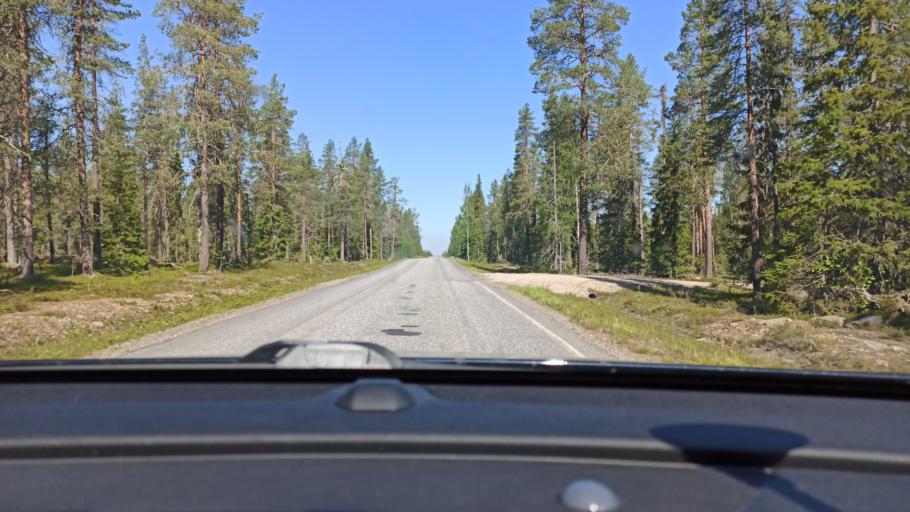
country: FI
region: Lapland
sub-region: Tunturi-Lappi
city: Kolari
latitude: 67.6729
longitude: 24.1473
